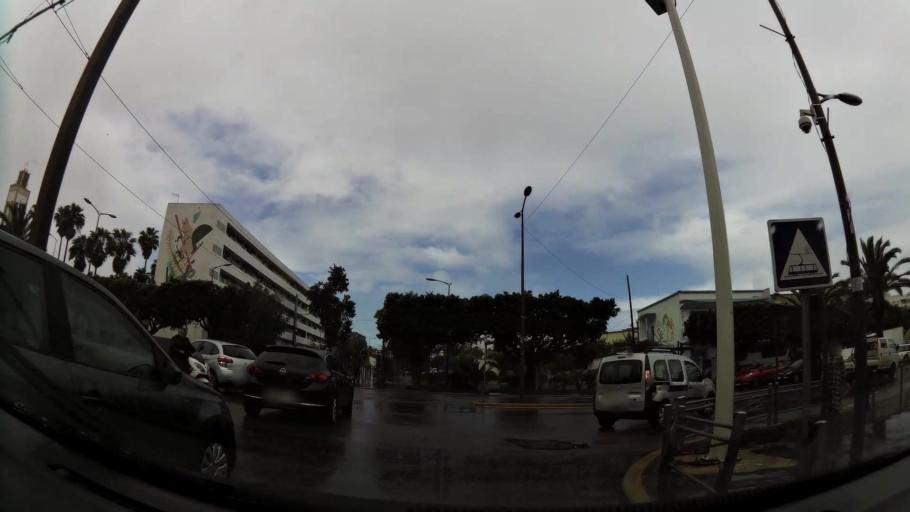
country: MA
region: Grand Casablanca
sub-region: Casablanca
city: Casablanca
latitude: 33.5709
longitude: -7.6356
